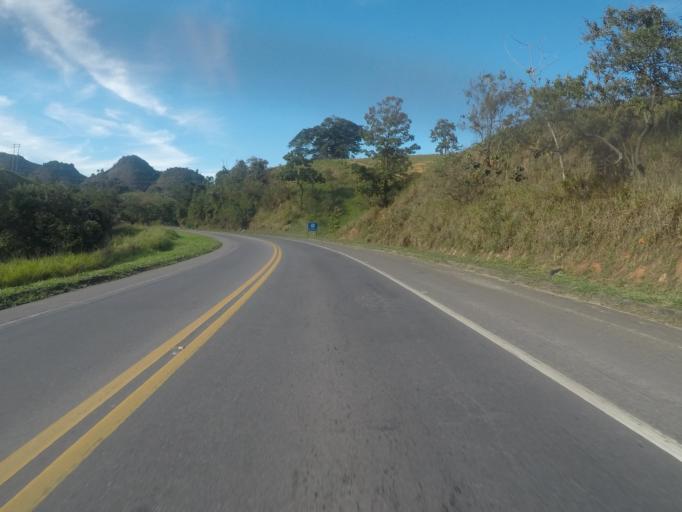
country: BR
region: Espirito Santo
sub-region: Ibiracu
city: Ibiracu
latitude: -19.8702
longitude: -40.4097
